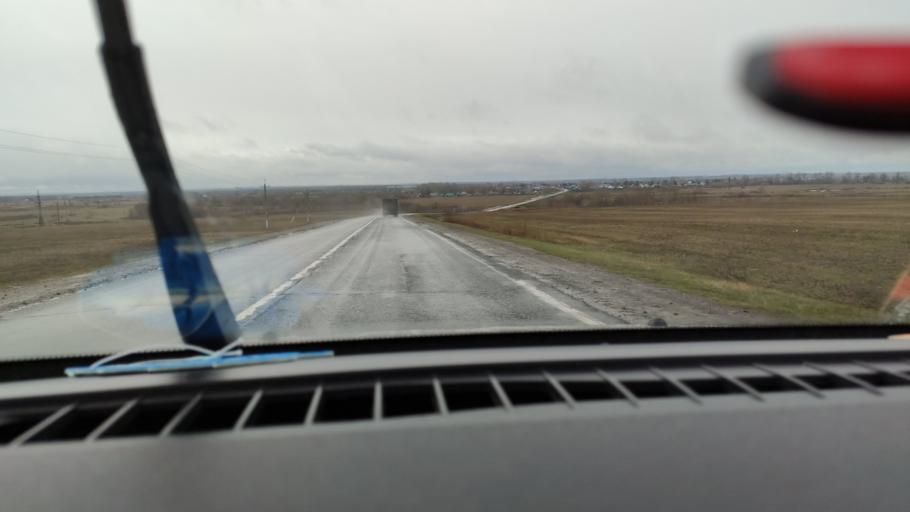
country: RU
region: Tatarstan
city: Nurlat
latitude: 54.5804
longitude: 50.8598
